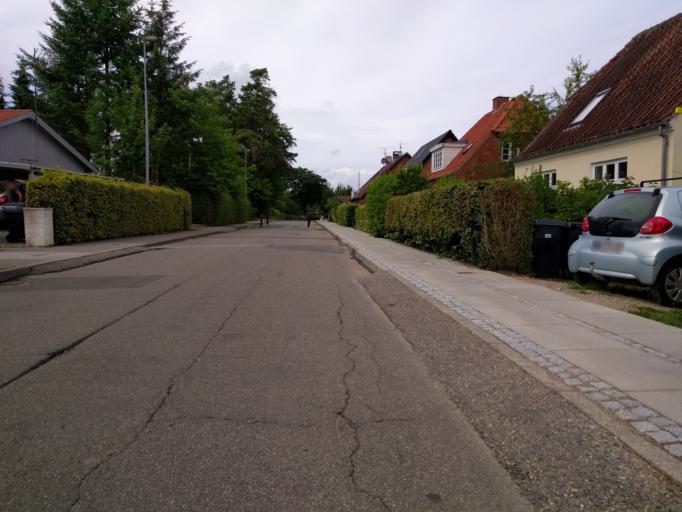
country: DK
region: Central Jutland
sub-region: Skanderborg Kommune
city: Ry
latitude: 56.0842
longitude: 9.7647
